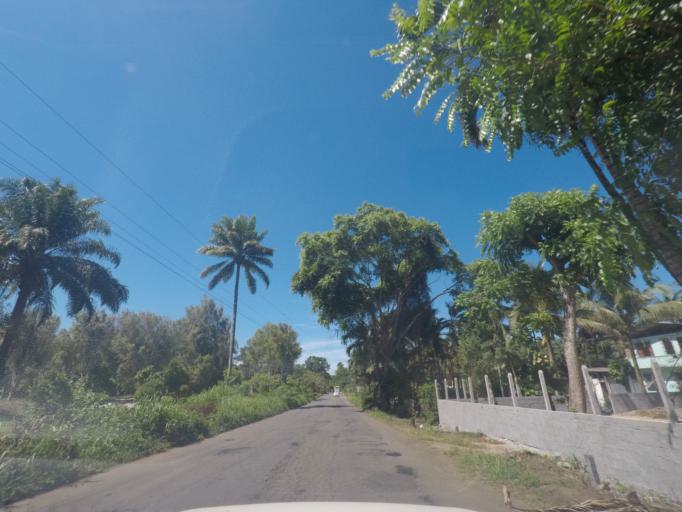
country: BR
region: Bahia
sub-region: Valenca
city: Valenca
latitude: -13.4274
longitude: -39.0776
